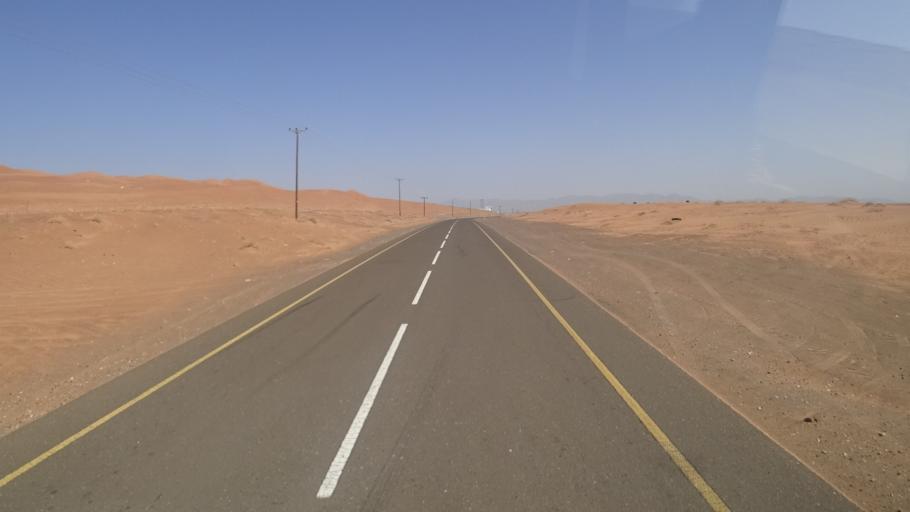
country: OM
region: Ash Sharqiyah
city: Al Qabil
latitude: 22.4929
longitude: 58.7152
